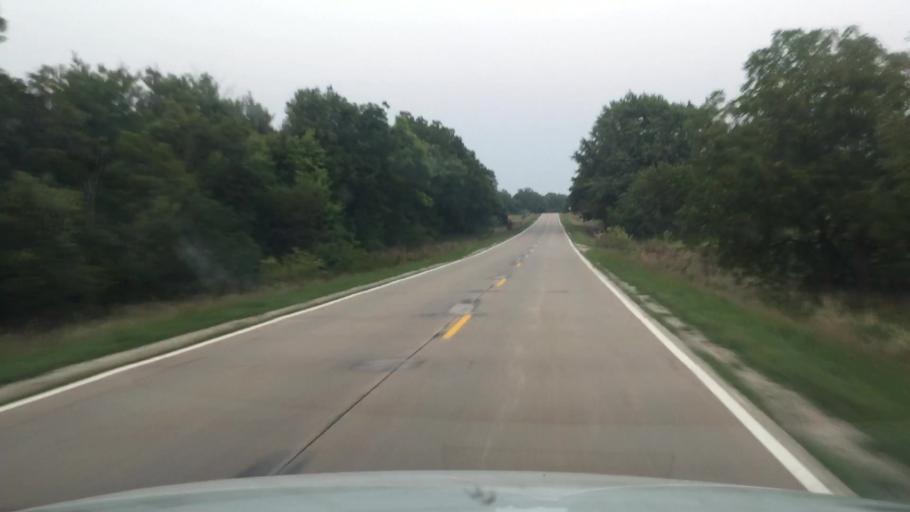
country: US
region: Iowa
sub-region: Warren County
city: Indianola
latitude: 41.1909
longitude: -93.6425
